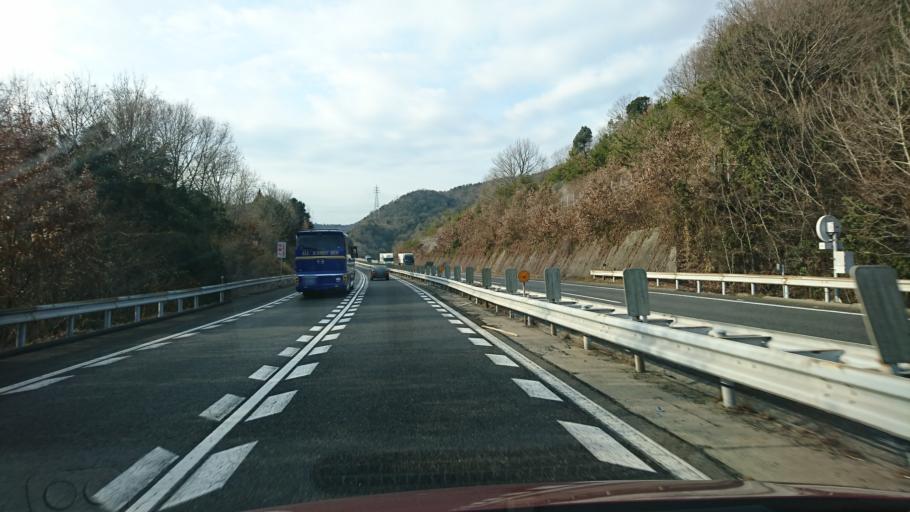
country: JP
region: Hyogo
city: Aioi
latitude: 34.8030
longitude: 134.4379
